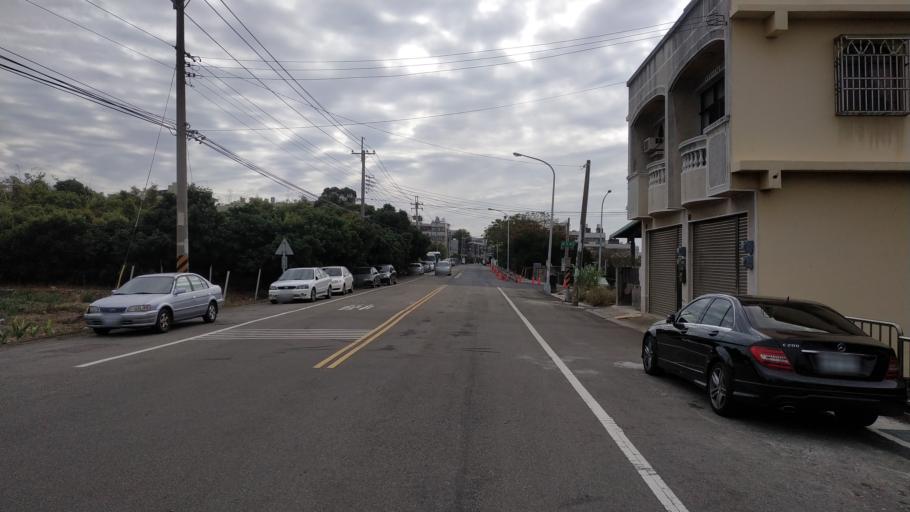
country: TW
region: Taiwan
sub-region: Taichung City
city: Taichung
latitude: 24.2172
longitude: 120.5747
